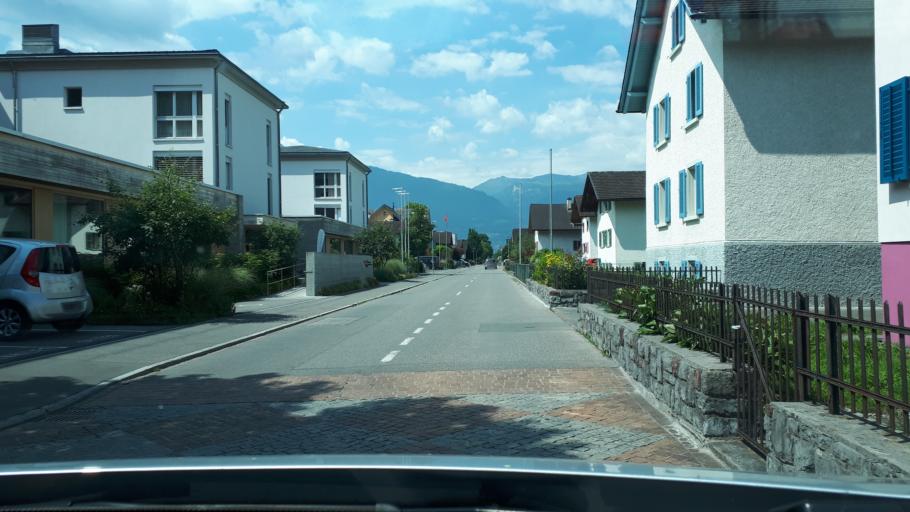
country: LI
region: Balzers
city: Balzers
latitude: 47.0647
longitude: 9.4969
